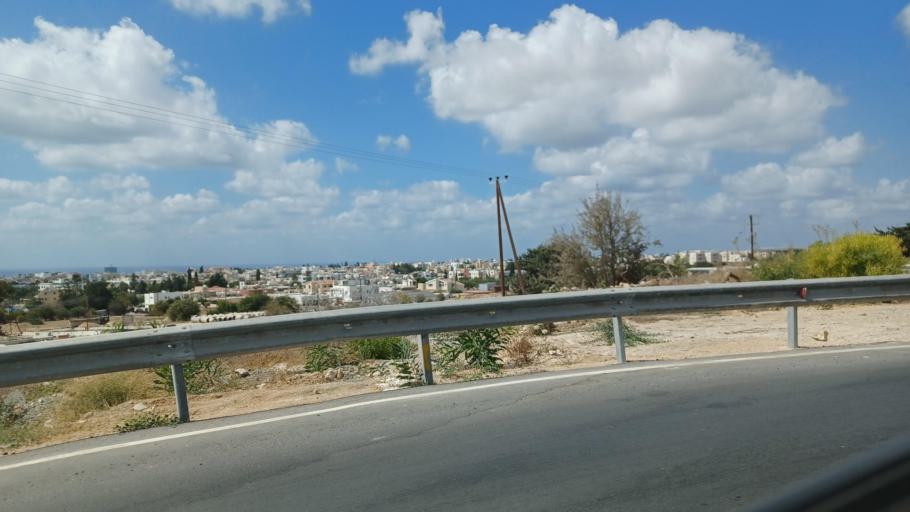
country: CY
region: Pafos
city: Paphos
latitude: 34.7657
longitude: 32.4580
